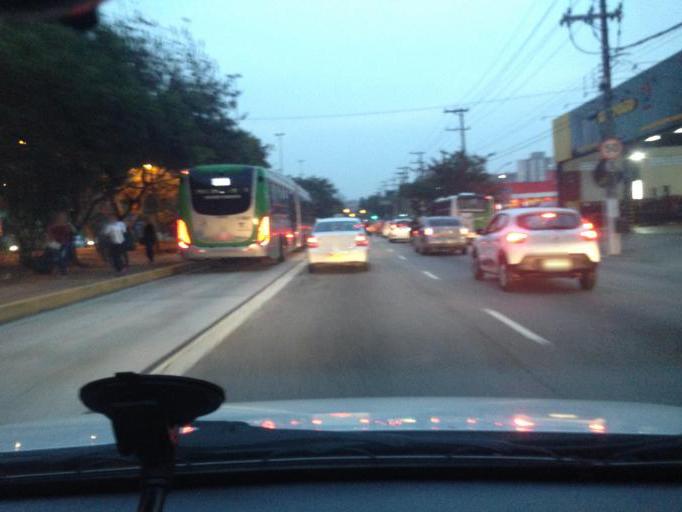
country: BR
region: Sao Paulo
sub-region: Sao Paulo
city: Sao Paulo
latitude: -23.5011
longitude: -46.7064
